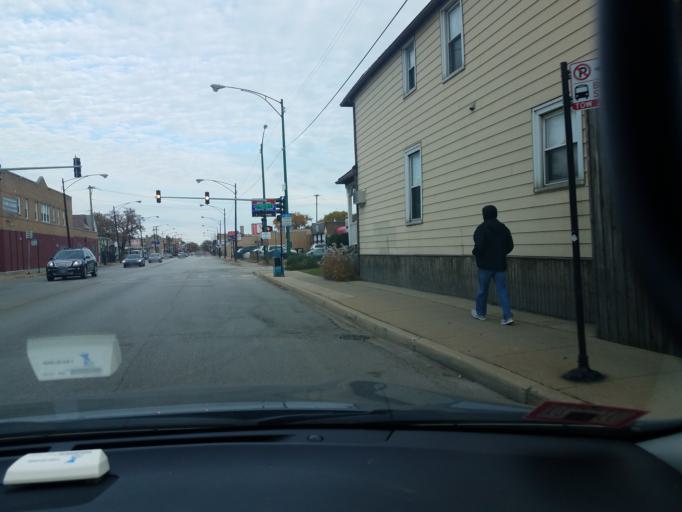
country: US
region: Illinois
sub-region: Cook County
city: Lincolnwood
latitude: 41.9609
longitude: -87.7332
